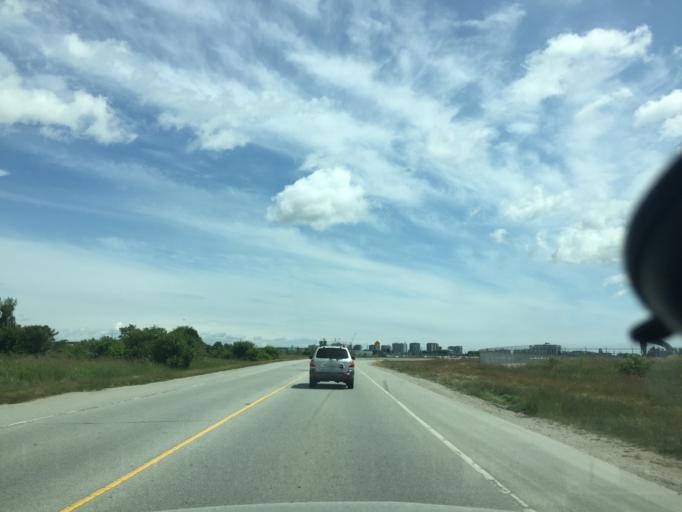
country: CA
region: British Columbia
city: Richmond
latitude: 49.2026
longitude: -123.1512
